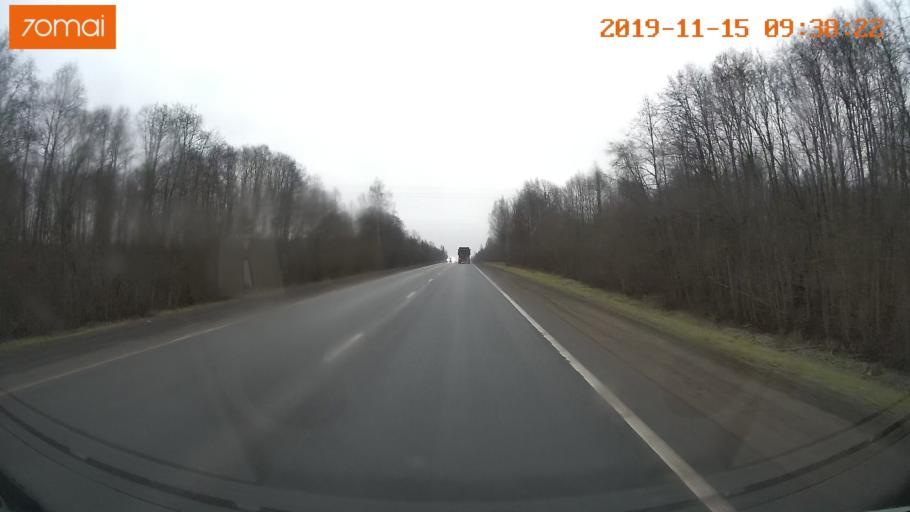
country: RU
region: Vologda
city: Sheksna
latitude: 59.2325
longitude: 38.4543
